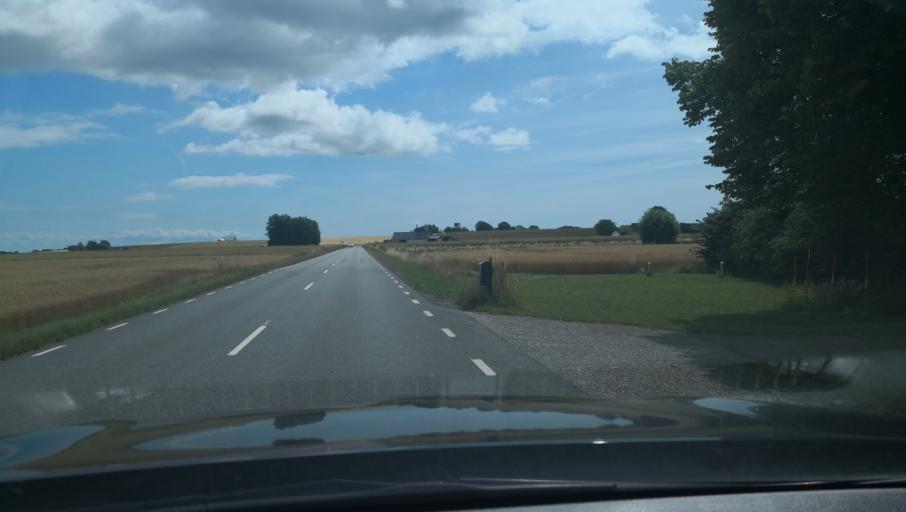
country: SE
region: Skane
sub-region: Ystads Kommun
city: Kopingebro
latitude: 55.4526
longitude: 14.1157
